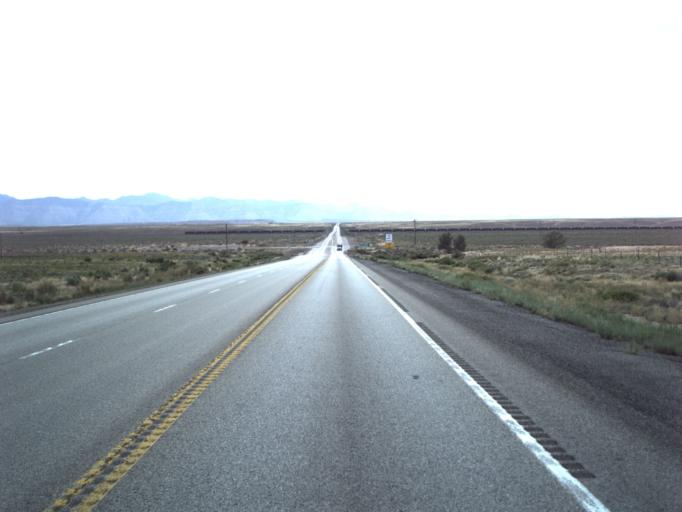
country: US
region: Utah
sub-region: Carbon County
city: Wellington
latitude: 39.5283
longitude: -110.5794
